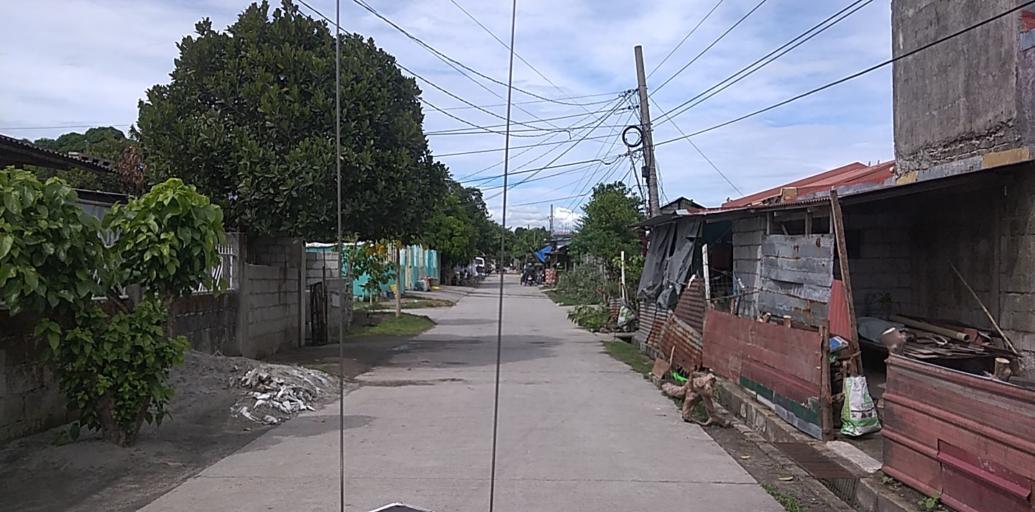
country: PH
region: Central Luzon
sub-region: Province of Pampanga
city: Manibaug Pasig
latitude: 15.1129
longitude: 120.5597
